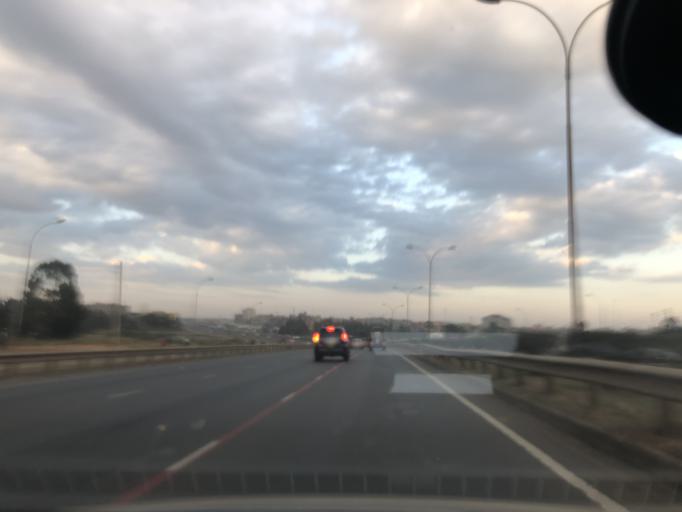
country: KE
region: Kiambu
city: Kiambu
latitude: -1.2103
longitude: 36.9092
